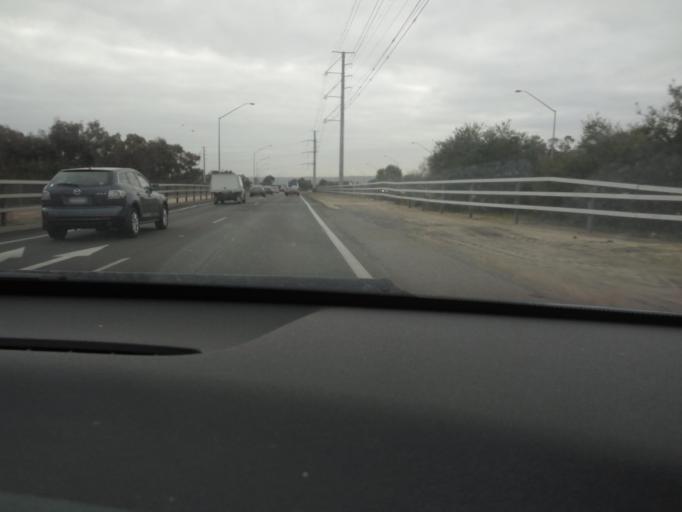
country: AU
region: Western Australia
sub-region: Gosnells
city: Langford
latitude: -32.0404
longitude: 115.9545
